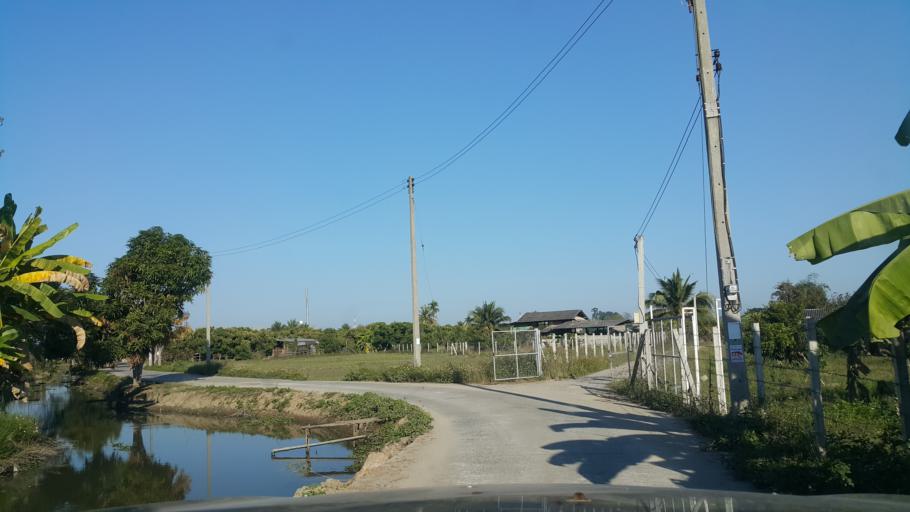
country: TH
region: Chiang Mai
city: Hang Dong
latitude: 18.6799
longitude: 98.9703
